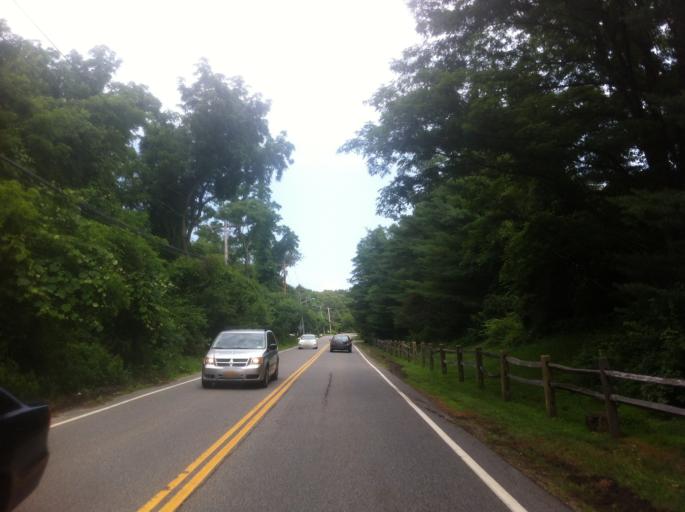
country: US
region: New York
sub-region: Nassau County
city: Oyster Bay Cove
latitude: 40.8541
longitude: -73.5112
